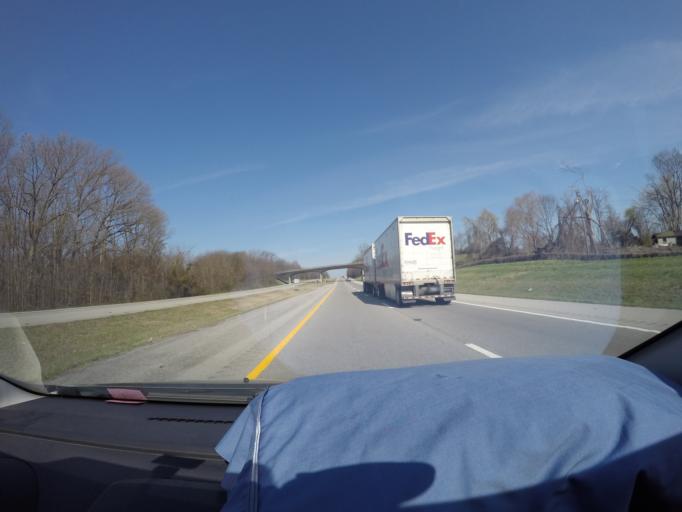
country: US
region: Tennessee
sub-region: Franklin County
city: Sewanee
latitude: 35.3324
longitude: -85.9333
